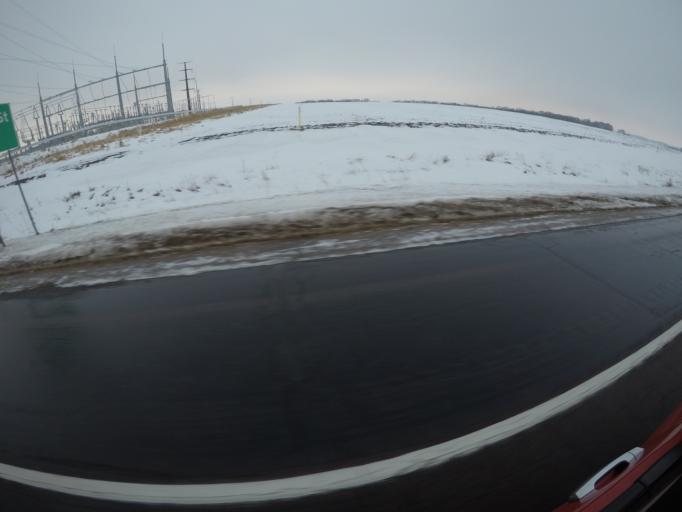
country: US
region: Minnesota
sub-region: Dakota County
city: Farmington
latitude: 44.6391
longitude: -92.9948
